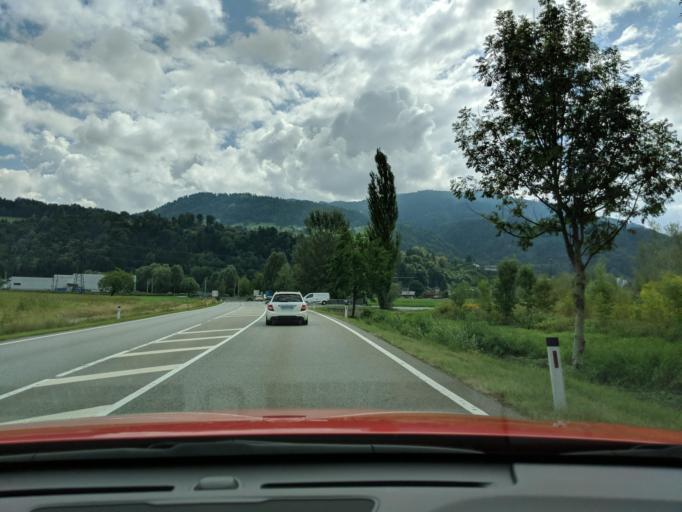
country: AT
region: Vorarlberg
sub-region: Politischer Bezirk Bregenz
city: Schwarzach
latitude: 47.4389
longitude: 9.7490
